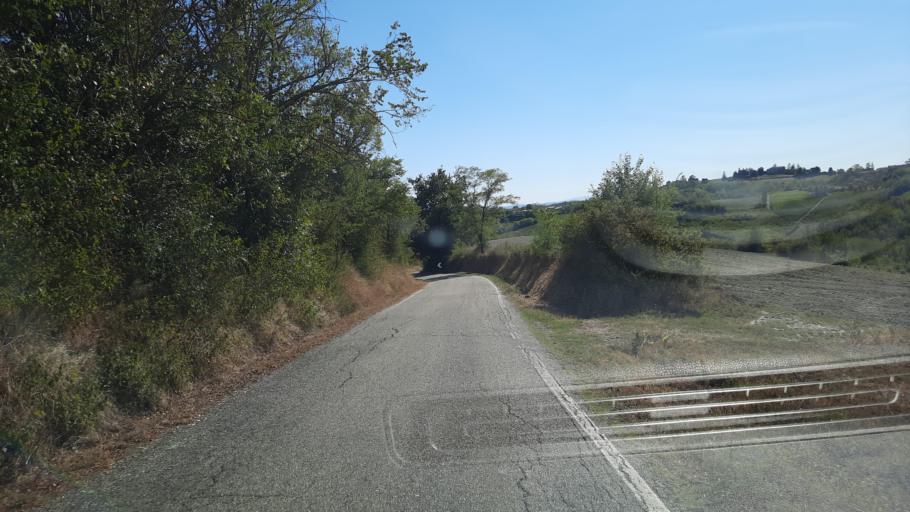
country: IT
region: Piedmont
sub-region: Provincia di Alessandria
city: Camagna Monferrato
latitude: 45.0085
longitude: 8.4332
